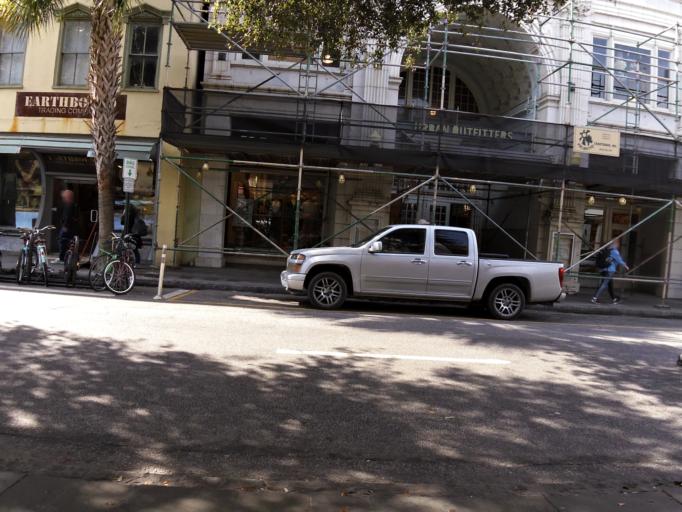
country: US
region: South Carolina
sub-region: Charleston County
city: Charleston
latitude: 32.7854
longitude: -79.9360
